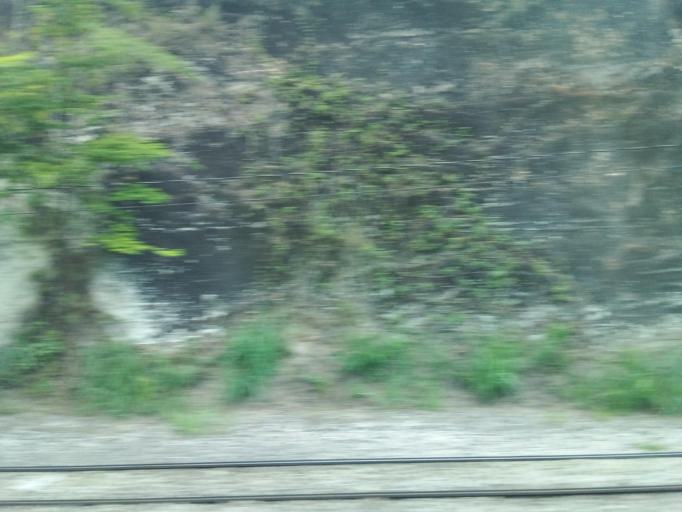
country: BR
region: Minas Gerais
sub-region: Joao Monlevade
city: Joao Monlevade
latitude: -19.8469
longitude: -43.1237
